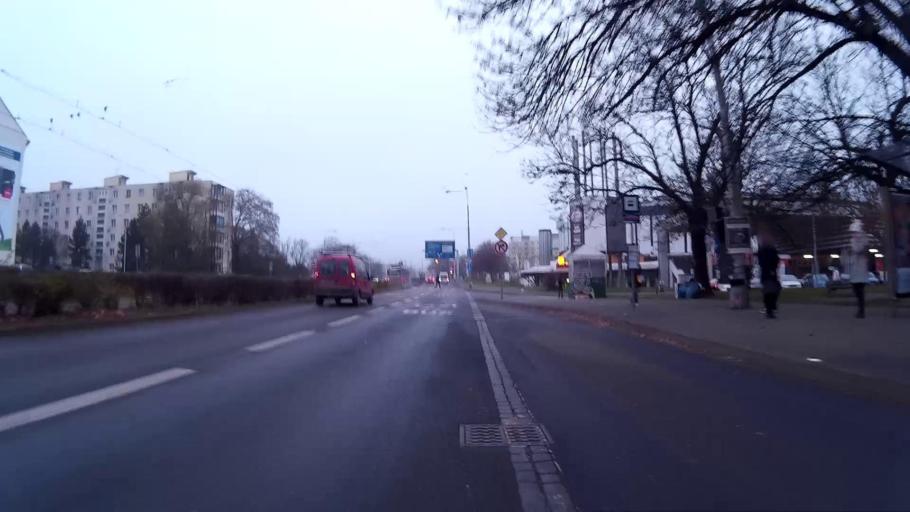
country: CZ
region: South Moravian
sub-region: Mesto Brno
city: Brno
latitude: 49.1860
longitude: 16.6038
